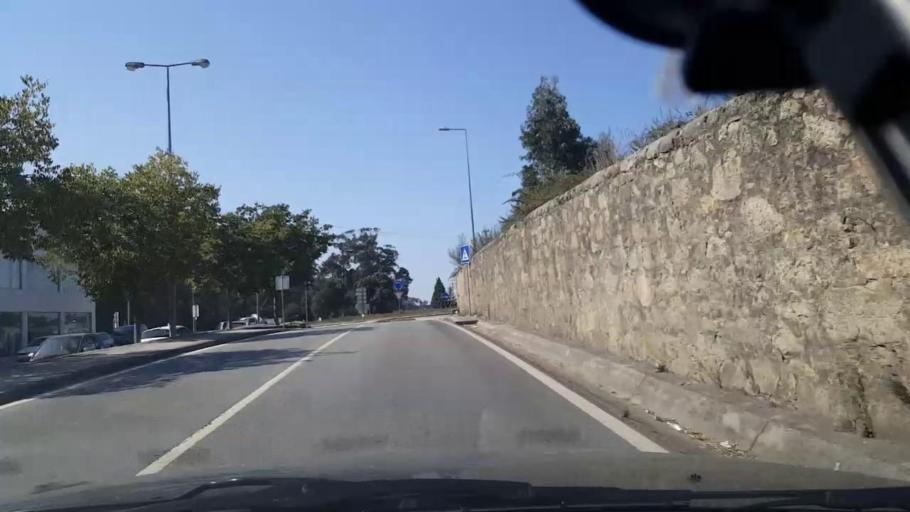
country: PT
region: Porto
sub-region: Povoa de Varzim
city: Pedroso
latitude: 41.3923
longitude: -8.6990
